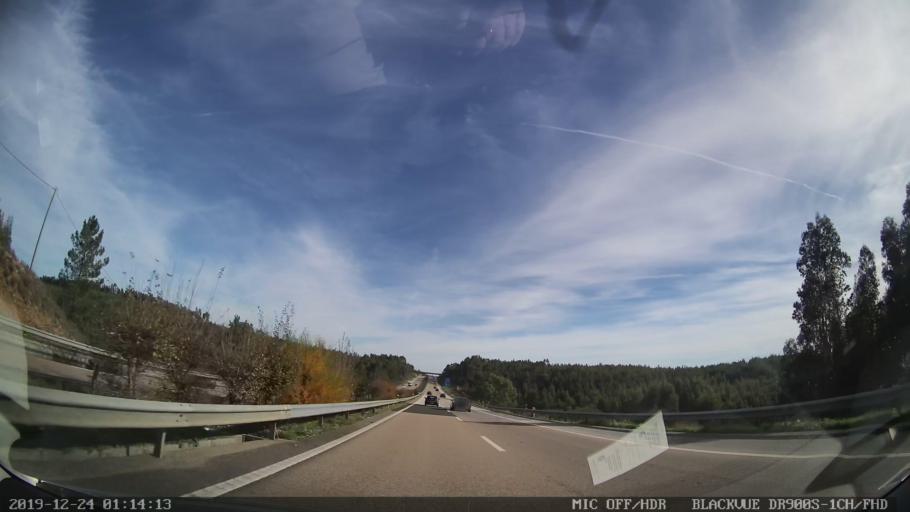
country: PT
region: Santarem
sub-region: Chamusca
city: Vila Nova da Barquinha
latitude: 39.4856
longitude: -8.4089
